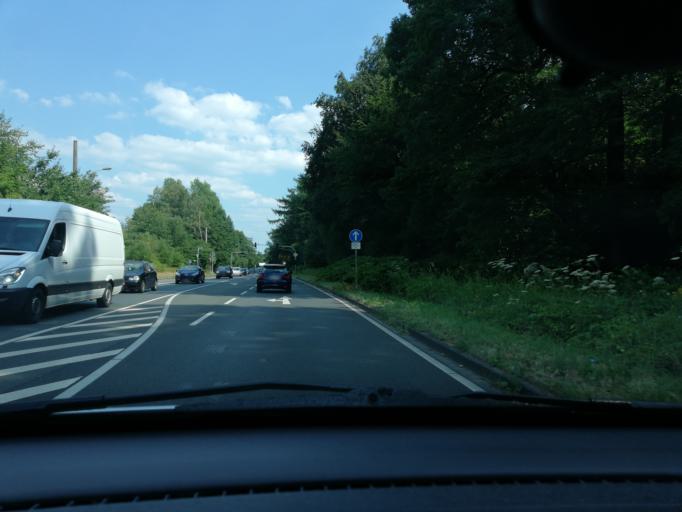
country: DE
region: North Rhine-Westphalia
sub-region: Regierungsbezirk Dusseldorf
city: Wuppertal
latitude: 51.2370
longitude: 7.2063
